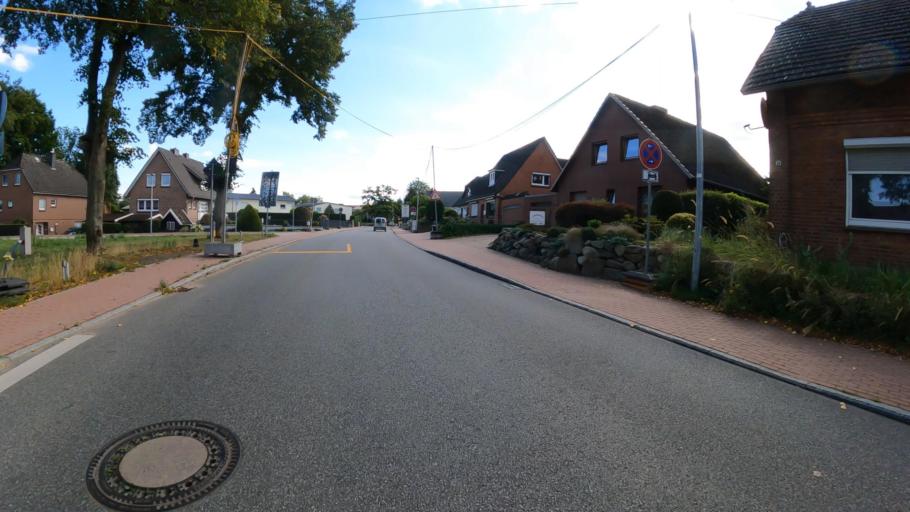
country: DE
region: Schleswig-Holstein
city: Todendorf
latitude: 53.6960
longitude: 10.3495
